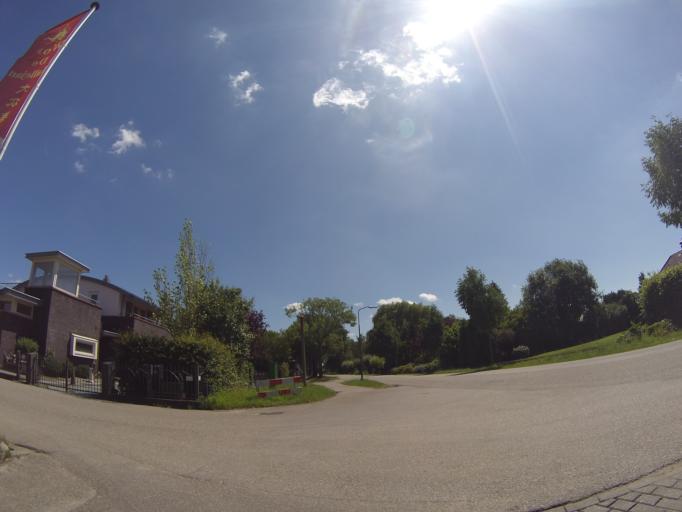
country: NL
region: Utrecht
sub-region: Stichtse Vecht
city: Maarssen
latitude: 52.1356
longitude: 5.0879
